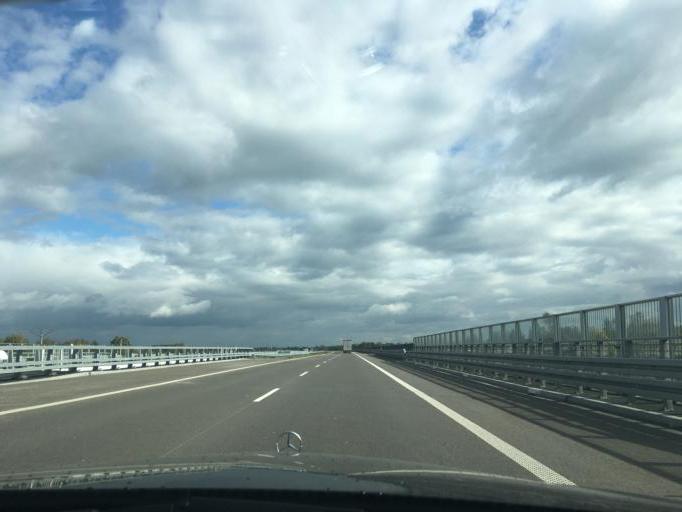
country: PL
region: Subcarpathian Voivodeship
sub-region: Powiat rzeszowski
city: Trzebownisko
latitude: 50.0927
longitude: 22.0711
